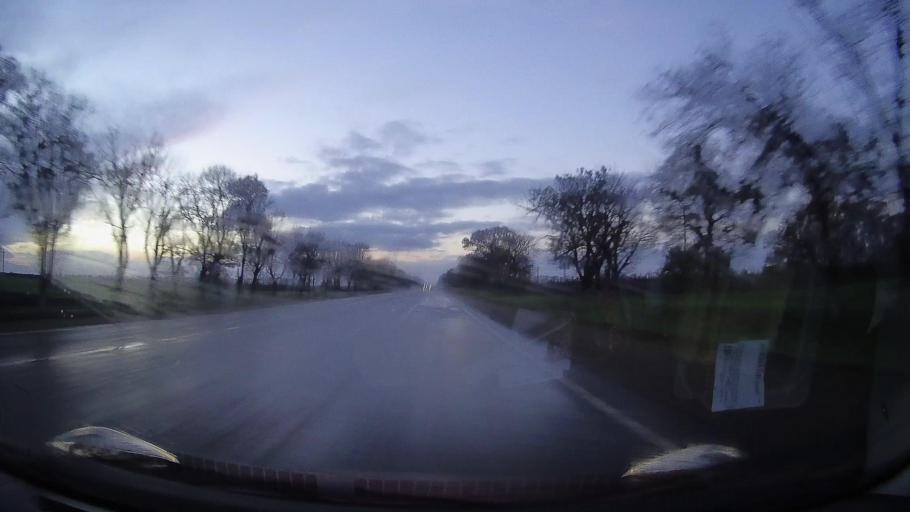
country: RU
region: Krasnodarskiy
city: Zavetnyy
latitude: 44.8892
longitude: 41.2102
